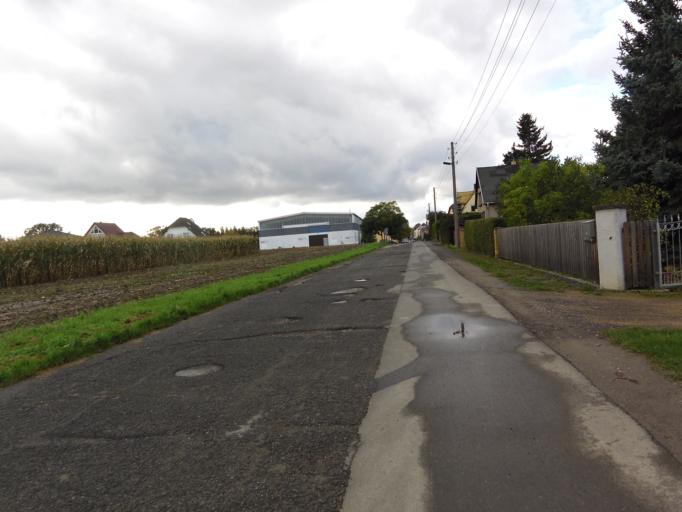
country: DE
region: Saxony
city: Grossposna
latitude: 51.3120
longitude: 12.4701
